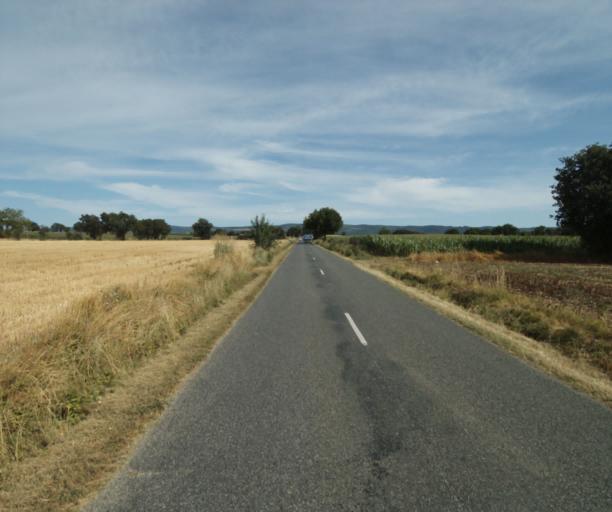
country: FR
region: Midi-Pyrenees
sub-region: Departement du Tarn
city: Soual
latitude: 43.5133
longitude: 2.0825
